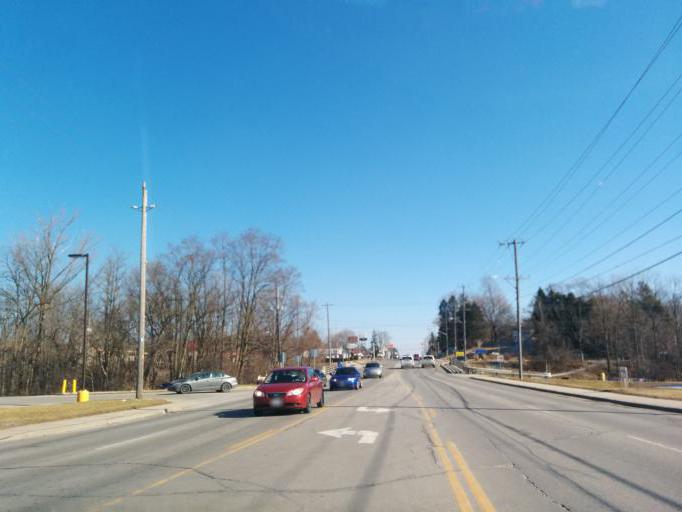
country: CA
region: Ontario
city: Norfolk County
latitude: 42.8464
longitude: -80.3058
